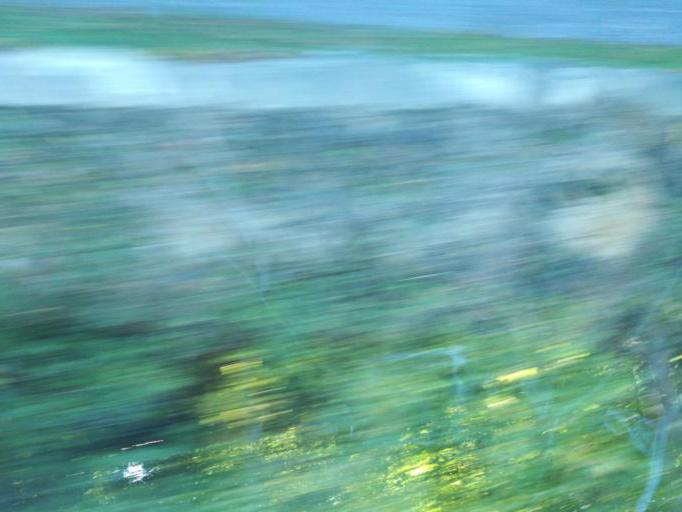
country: RO
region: Brasov
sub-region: Comuna Dumbravita
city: Dumbravita
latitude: 45.7614
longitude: 25.3833
